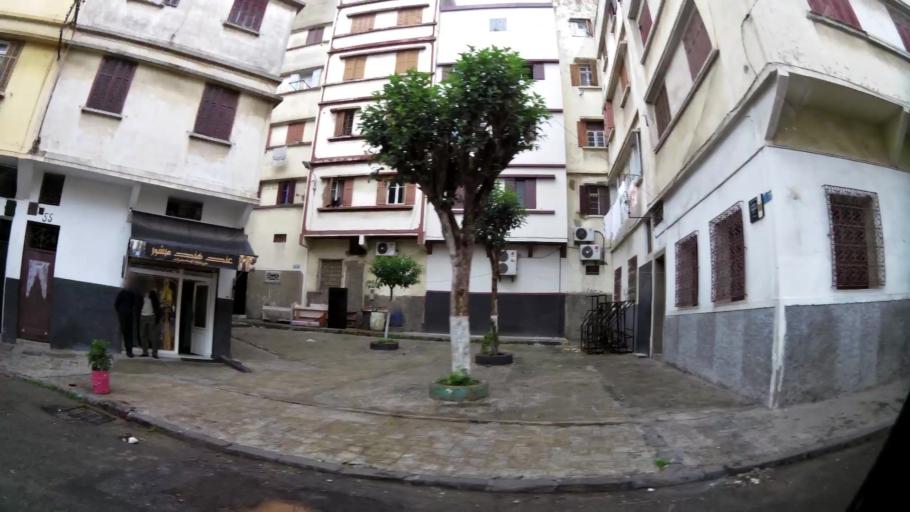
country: MA
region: Grand Casablanca
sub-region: Casablanca
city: Casablanca
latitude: 33.5685
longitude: -7.5898
